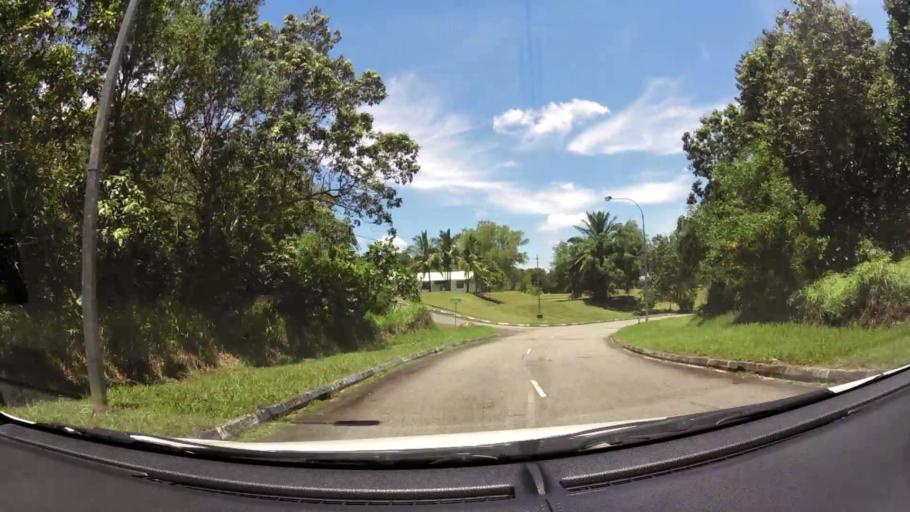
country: BN
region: Brunei and Muara
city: Bandar Seri Begawan
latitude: 4.9192
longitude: 114.9595
